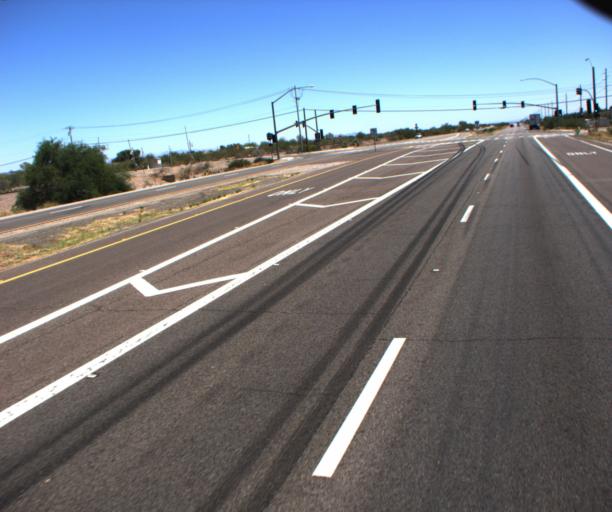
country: US
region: Arizona
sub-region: Maricopa County
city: Sun City West
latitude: 33.7790
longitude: -112.5303
